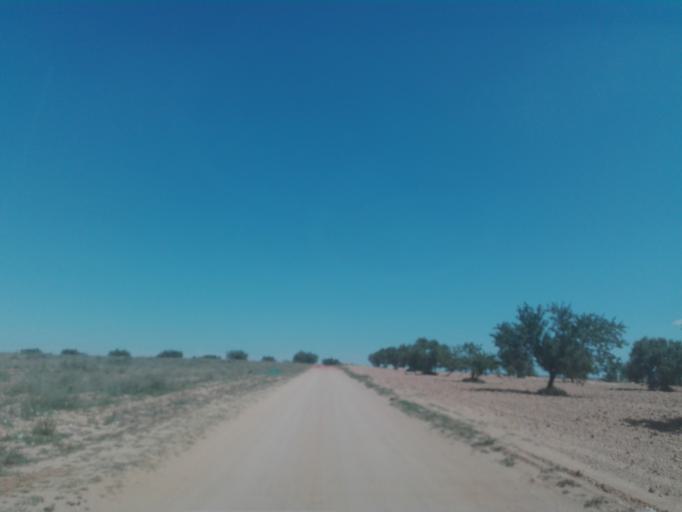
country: TN
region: Safaqis
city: Sfax
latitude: 34.7297
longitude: 10.4313
